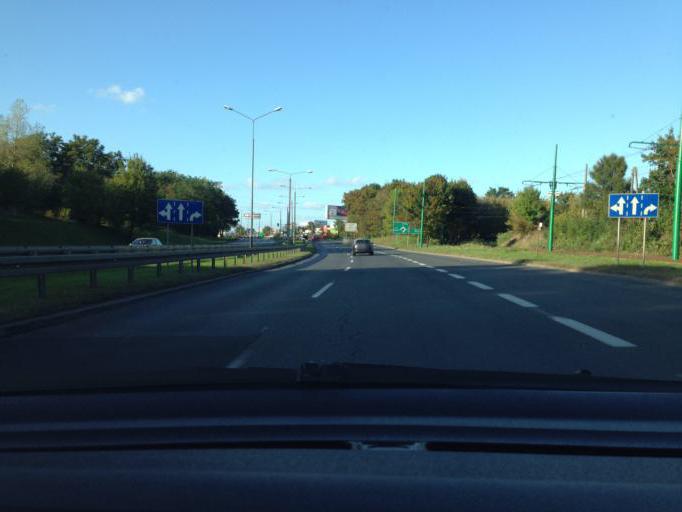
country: PL
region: Greater Poland Voivodeship
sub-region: Poznan
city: Poznan
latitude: 52.4399
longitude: 16.9099
